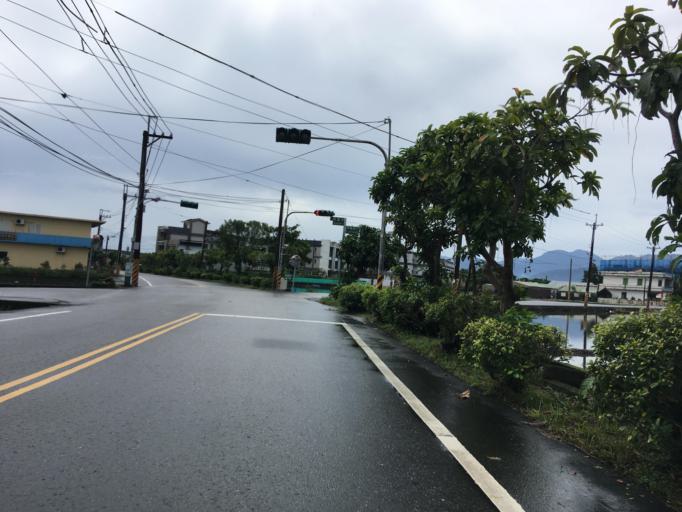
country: TW
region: Taiwan
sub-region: Yilan
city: Yilan
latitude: 24.6656
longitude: 121.7939
